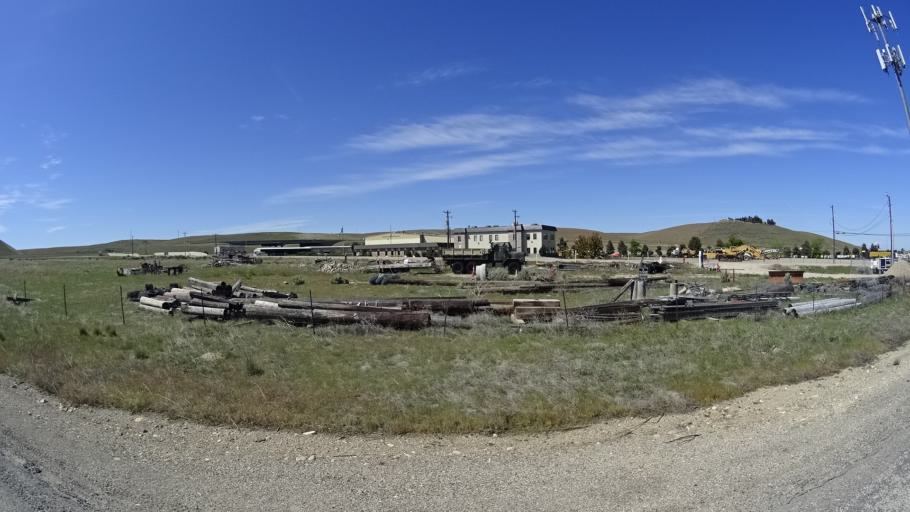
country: US
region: Idaho
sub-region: Ada County
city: Boise
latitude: 43.5112
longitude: -116.1414
